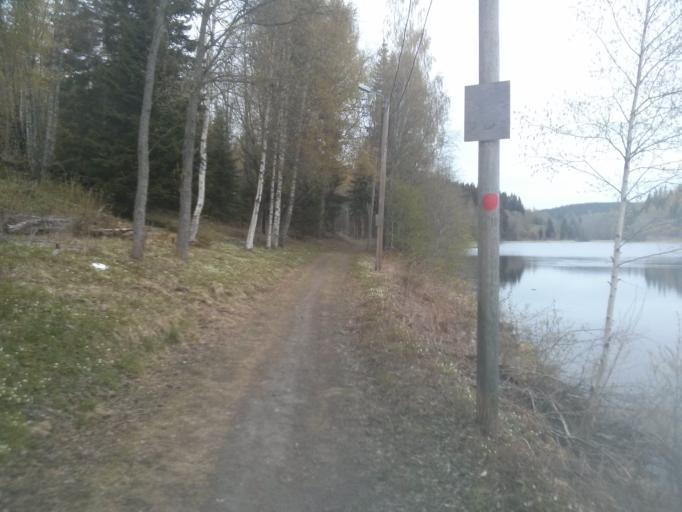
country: SE
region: Vaesternorrland
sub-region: Sundsvalls Kommun
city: Nolby
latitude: 62.2973
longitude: 17.3567
